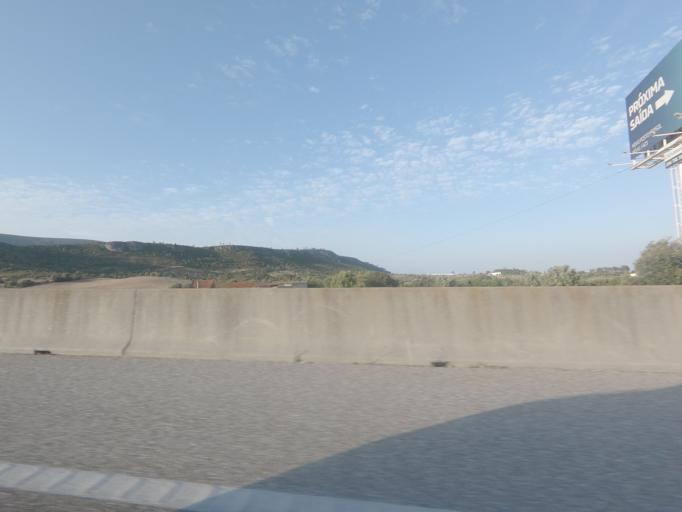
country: PT
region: Santarem
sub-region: Alcanena
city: Alcanena
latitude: 39.4851
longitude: -8.6384
